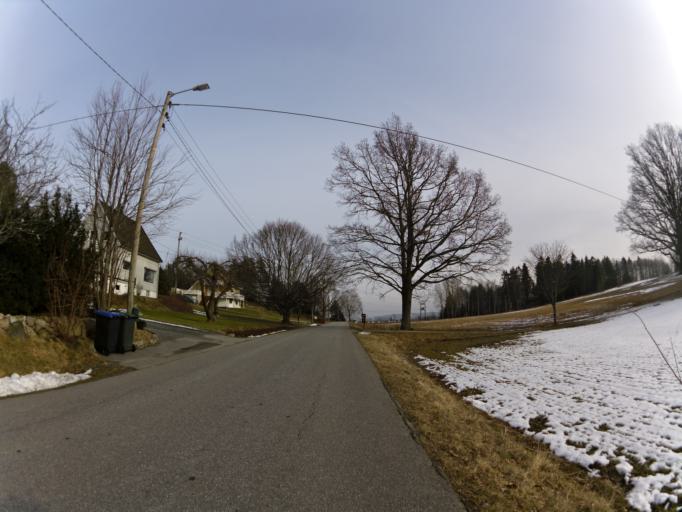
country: NO
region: Ostfold
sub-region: Fredrikstad
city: Fredrikstad
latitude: 59.2730
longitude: 11.0077
